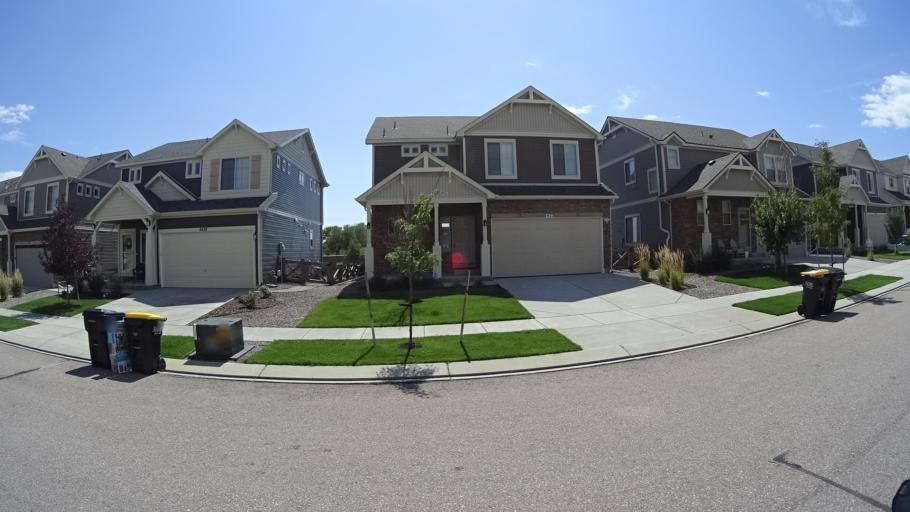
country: US
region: Colorado
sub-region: El Paso County
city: Cimarron Hills
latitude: 38.9273
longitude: -104.6697
